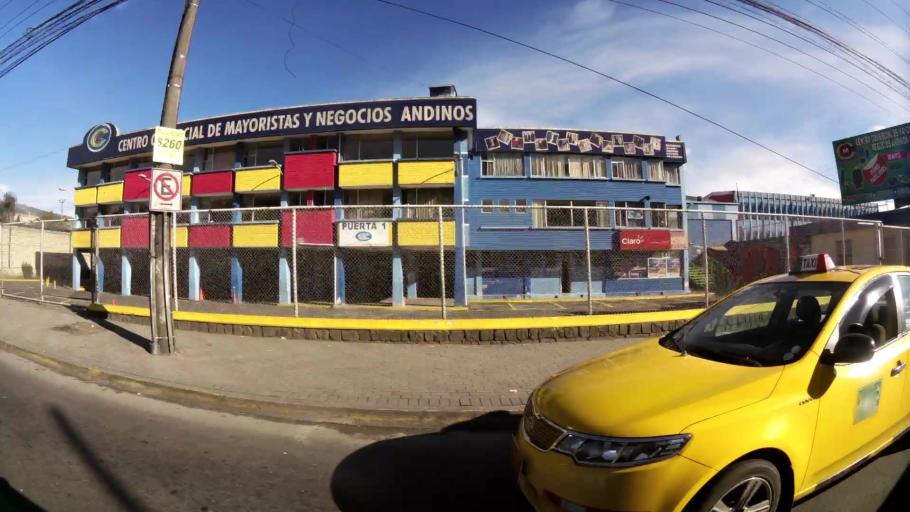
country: EC
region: Pichincha
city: Quito
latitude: -0.2796
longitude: -78.5328
